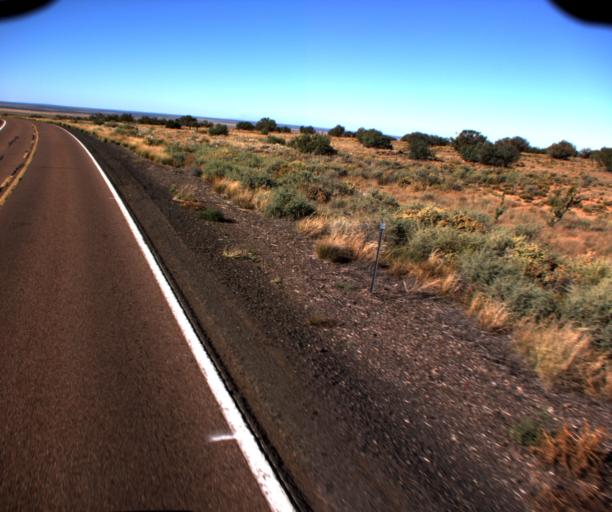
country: US
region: Arizona
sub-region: Navajo County
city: Snowflake
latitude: 34.6428
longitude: -110.3553
